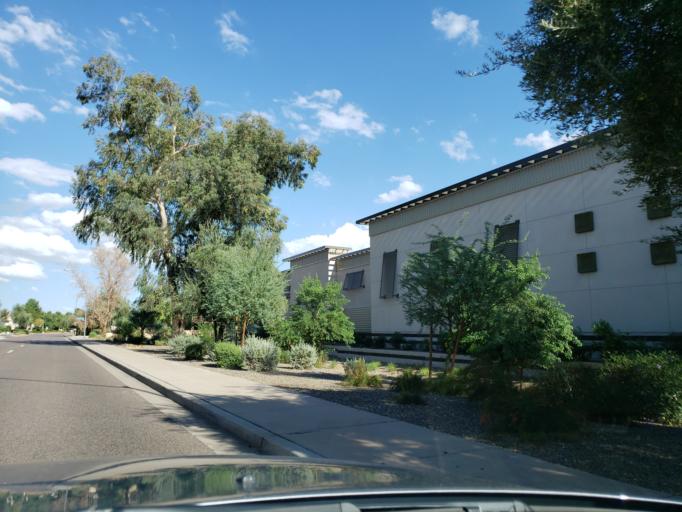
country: US
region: Arizona
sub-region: Maricopa County
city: Scottsdale
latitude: 33.5708
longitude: -111.8802
